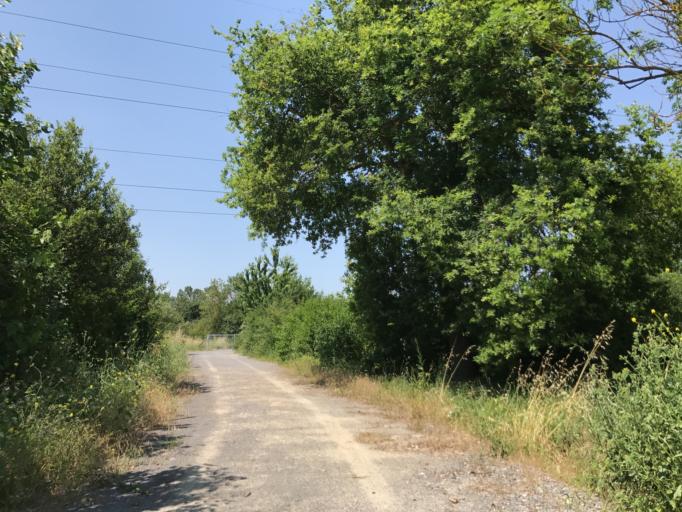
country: ES
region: Basque Country
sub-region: Provincia de Alava
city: Gasteiz / Vitoria
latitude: 42.8761
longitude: -2.6878
